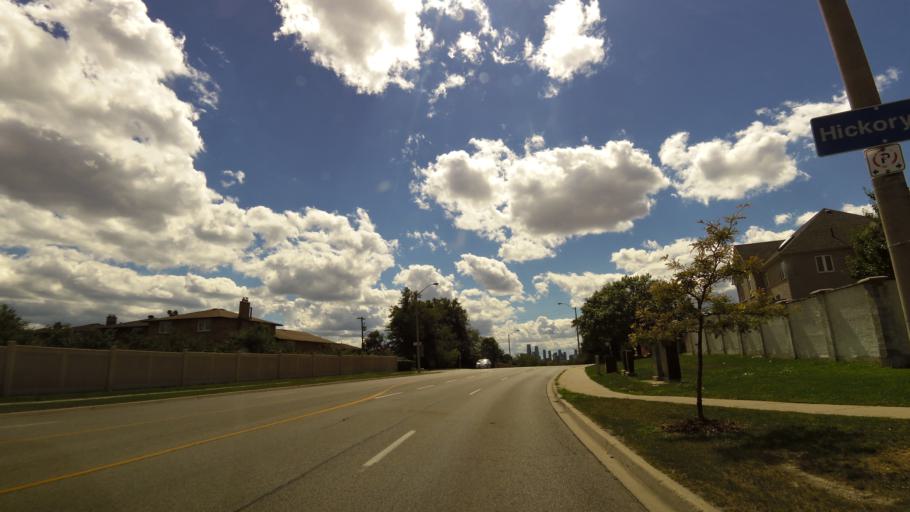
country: CA
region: Ontario
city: Etobicoke
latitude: 43.6251
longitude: -79.6085
